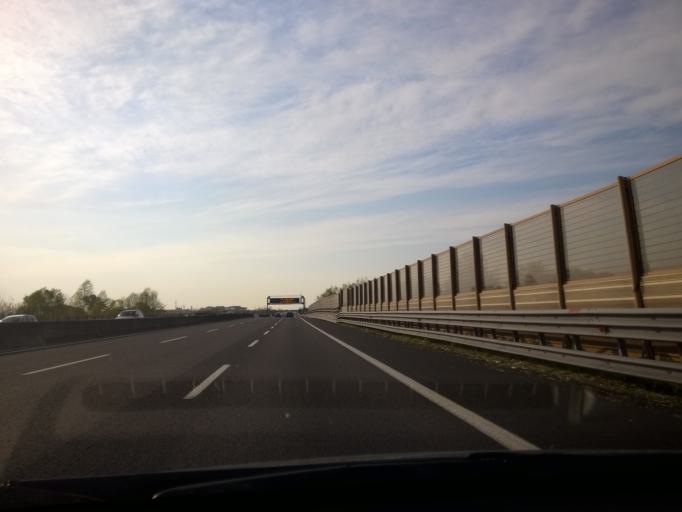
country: IT
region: Emilia-Romagna
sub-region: Forli-Cesena
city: Santa Maria Nuova
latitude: 44.1914
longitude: 12.2344
